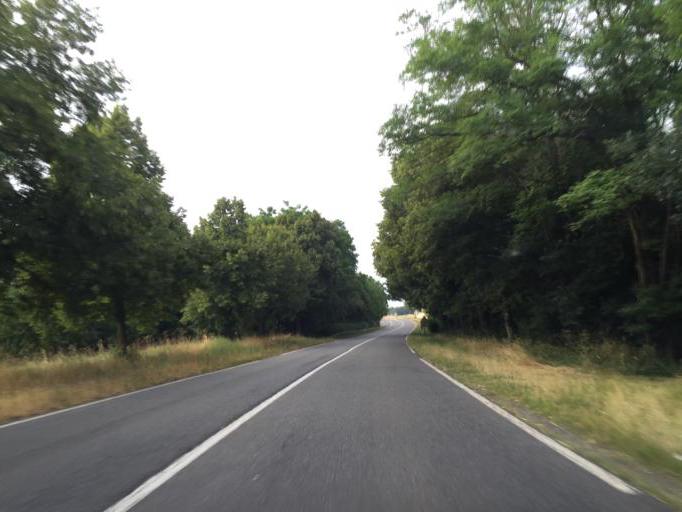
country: FR
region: Auvergne
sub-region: Departement de l'Allier
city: Saint-Germain-des-Fosses
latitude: 46.2614
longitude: 3.4299
